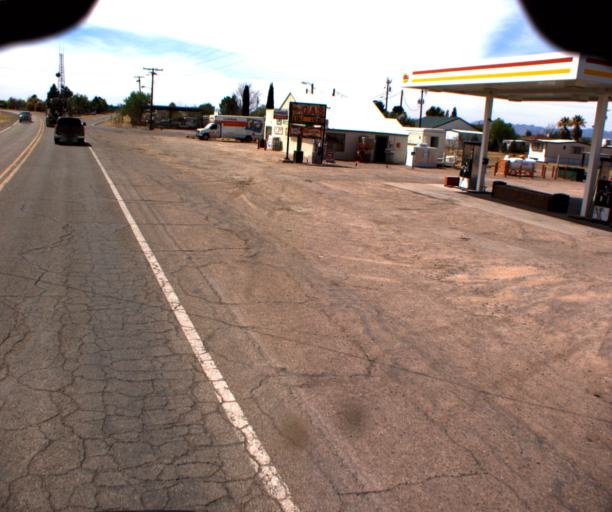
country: US
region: Arizona
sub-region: Cochise County
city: Bisbee
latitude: 31.6828
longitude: -109.6874
